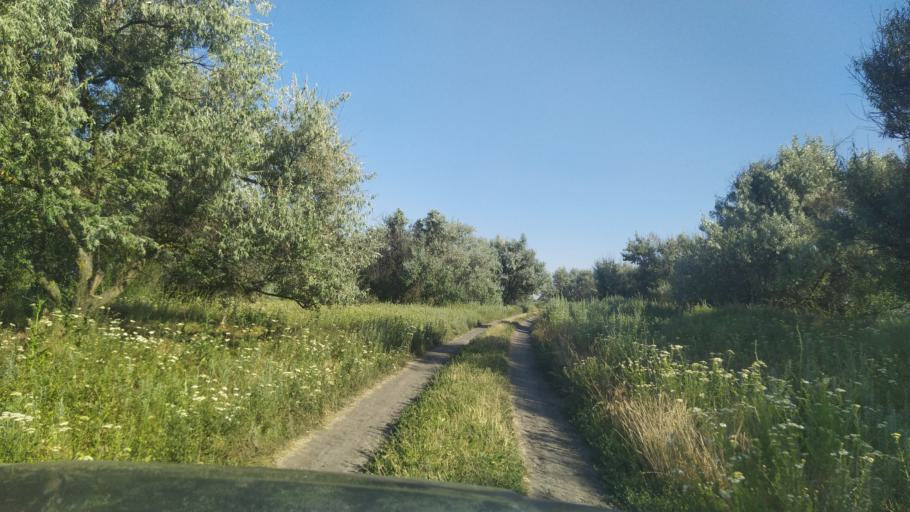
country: RU
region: Rostov
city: Kuleshovka
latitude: 47.1345
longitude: 39.6416
